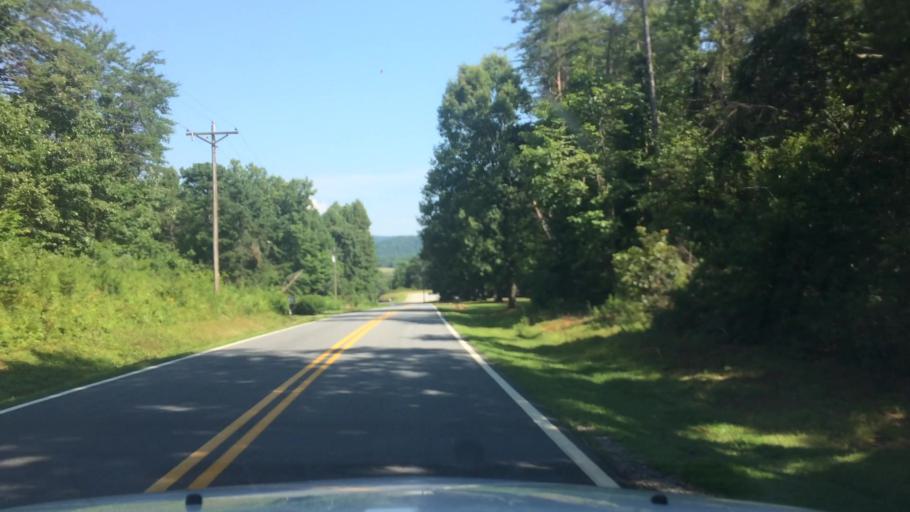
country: US
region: North Carolina
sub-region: Alexander County
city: Taylorsville
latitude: 35.9531
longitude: -81.2677
